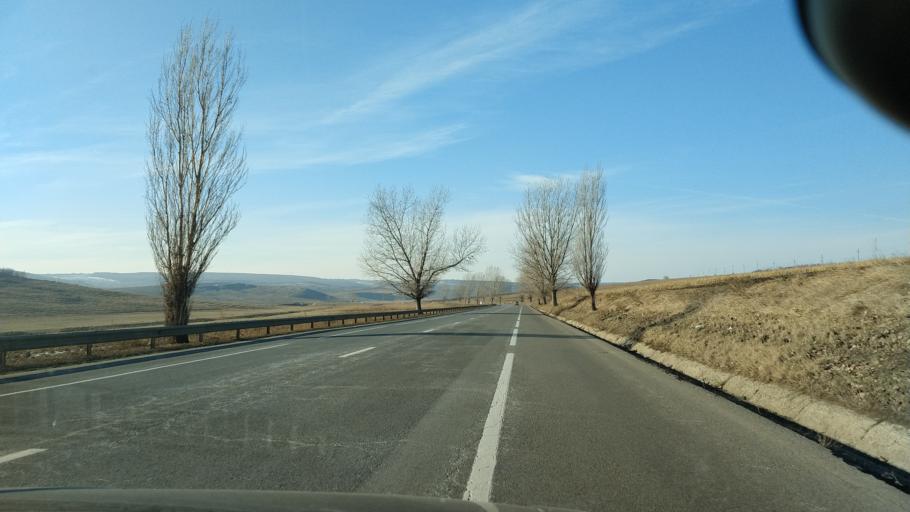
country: RO
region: Iasi
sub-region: Comuna Targu Frumos
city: Targu Frumos
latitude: 47.1975
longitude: 26.9858
